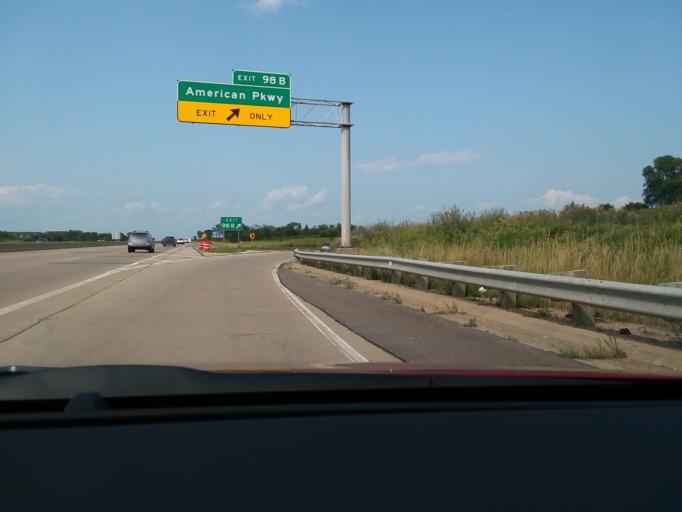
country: US
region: Wisconsin
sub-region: Dane County
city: Sun Prairie
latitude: 43.1460
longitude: -89.2849
